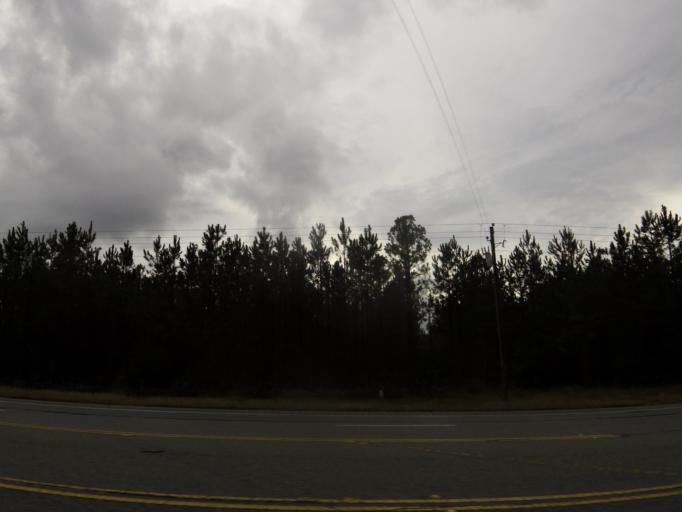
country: US
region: Georgia
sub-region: Wayne County
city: Jesup
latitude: 31.5559
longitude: -81.8220
